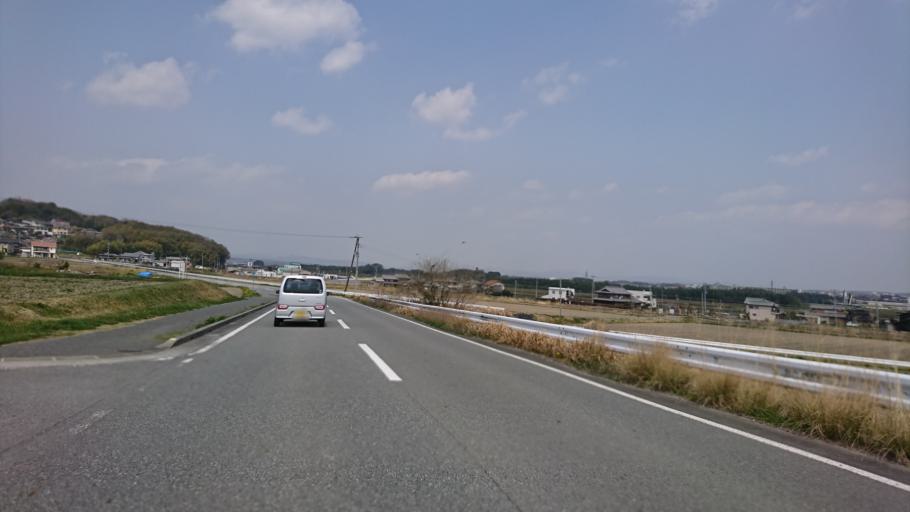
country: JP
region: Hyogo
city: Ono
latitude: 34.8379
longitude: 134.9107
